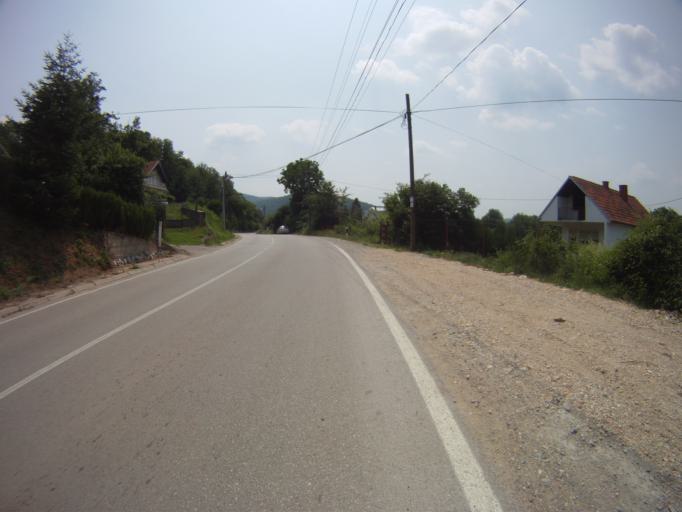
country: RS
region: Central Serbia
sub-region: Nisavski Okrug
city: Gadzin Han
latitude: 43.2281
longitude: 22.0323
